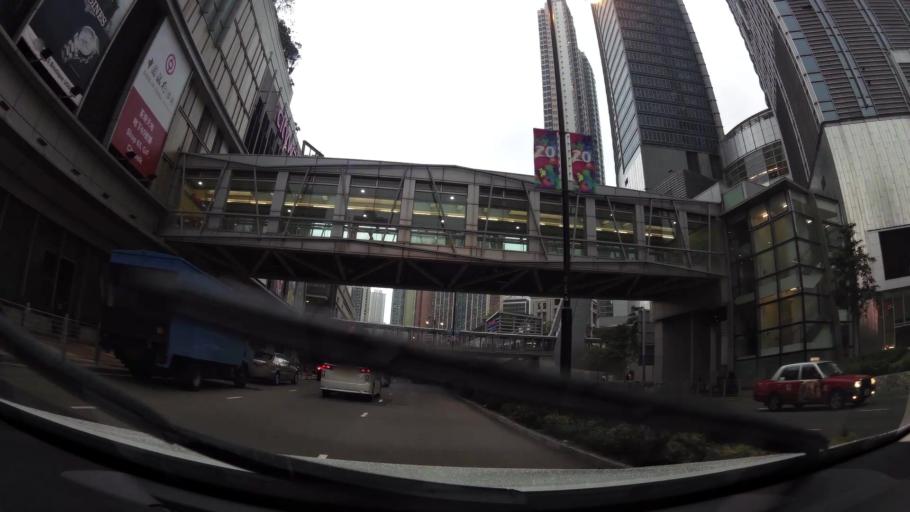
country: HK
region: Tsuen Wan
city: Tsuen Wan
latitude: 22.3697
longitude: 114.1129
